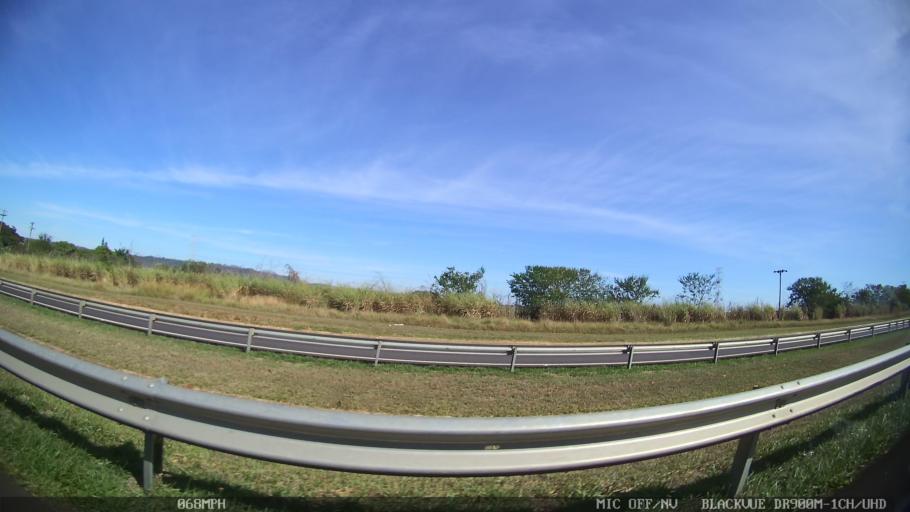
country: BR
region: Sao Paulo
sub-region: Pirassununga
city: Pirassununga
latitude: -21.9828
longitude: -47.4511
